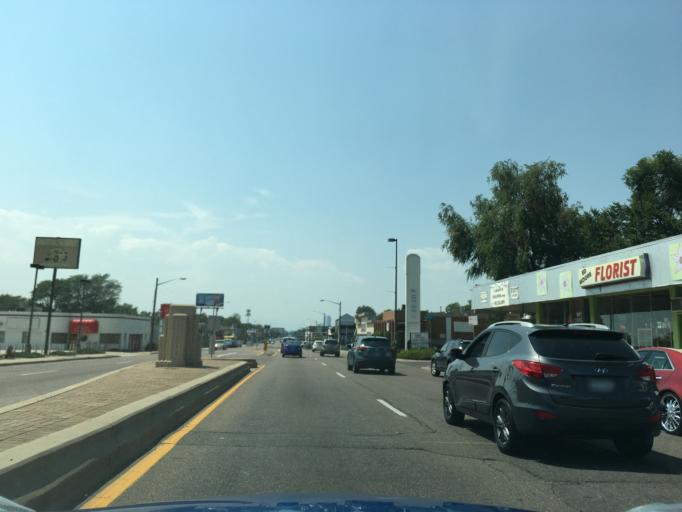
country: US
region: Colorado
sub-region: Arapahoe County
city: Glendale
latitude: 39.7402
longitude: -104.9168
